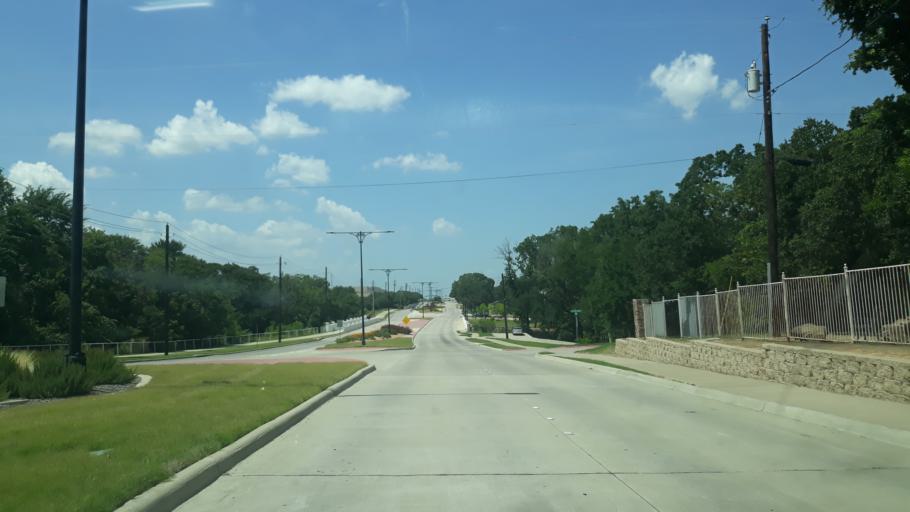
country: US
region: Texas
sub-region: Dallas County
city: Coppell
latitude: 32.9658
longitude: -97.0150
